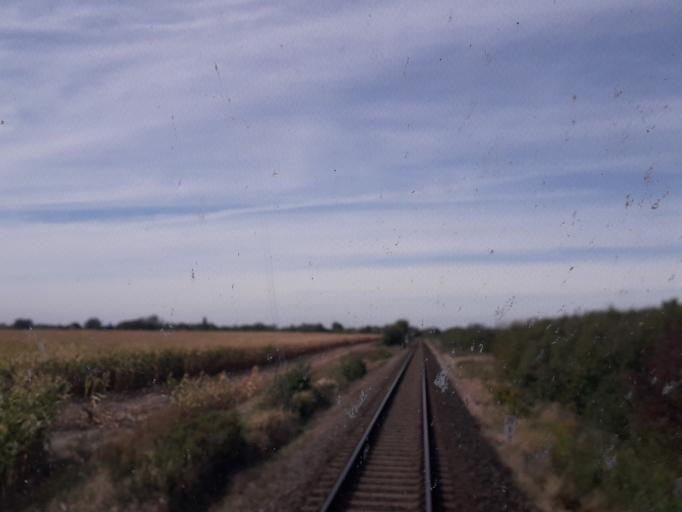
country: DE
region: Brandenburg
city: Velten
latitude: 52.7147
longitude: 13.1276
